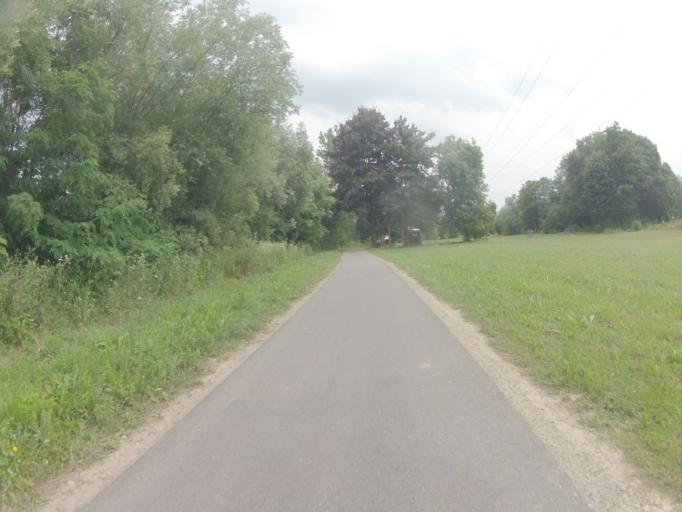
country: PL
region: Lesser Poland Voivodeship
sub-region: Powiat nowosadecki
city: Stary Sacz
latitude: 49.5409
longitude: 20.6566
